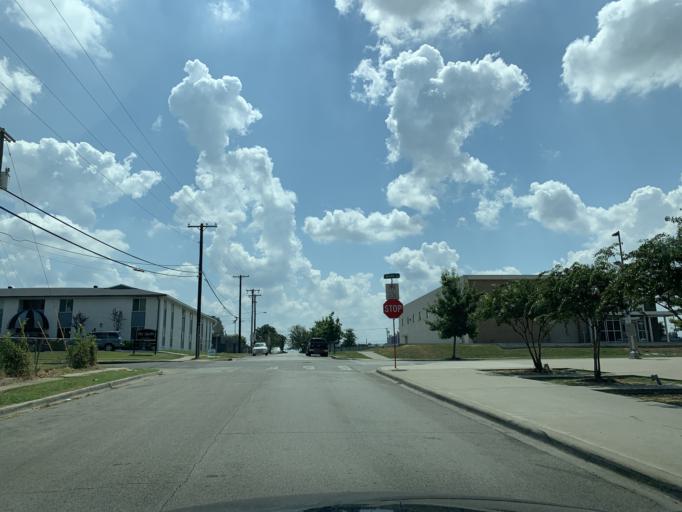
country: US
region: Texas
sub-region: Dallas County
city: Dallas
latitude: 32.7484
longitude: -96.8197
